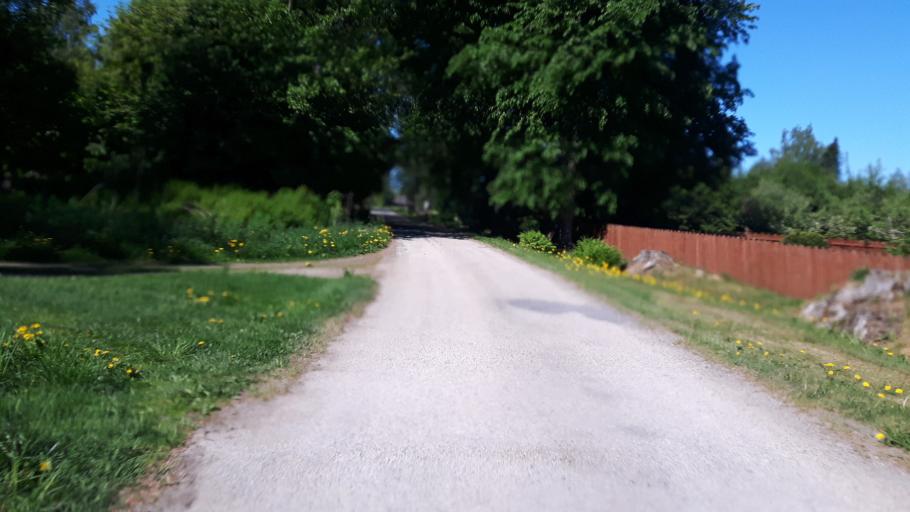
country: EE
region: Harju
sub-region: Loksa linn
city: Loksa
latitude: 59.5588
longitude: 25.7980
